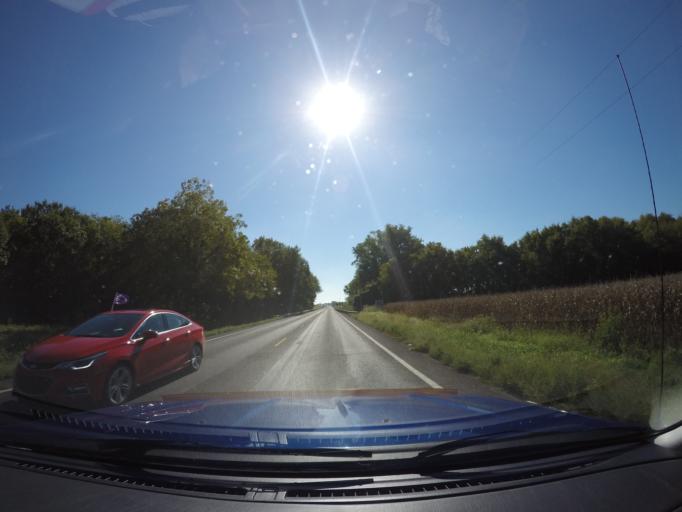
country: US
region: Kansas
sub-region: Pottawatomie County
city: Saint Marys
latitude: 39.2056
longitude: -96.0986
